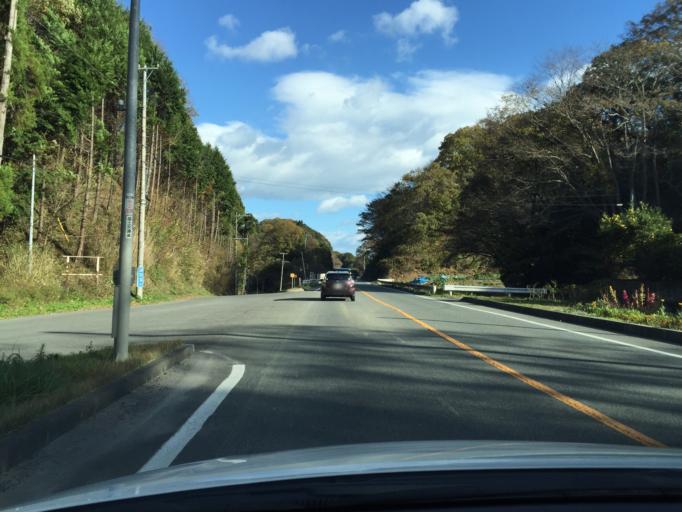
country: JP
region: Fukushima
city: Iwaki
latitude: 37.1873
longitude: 140.9963
